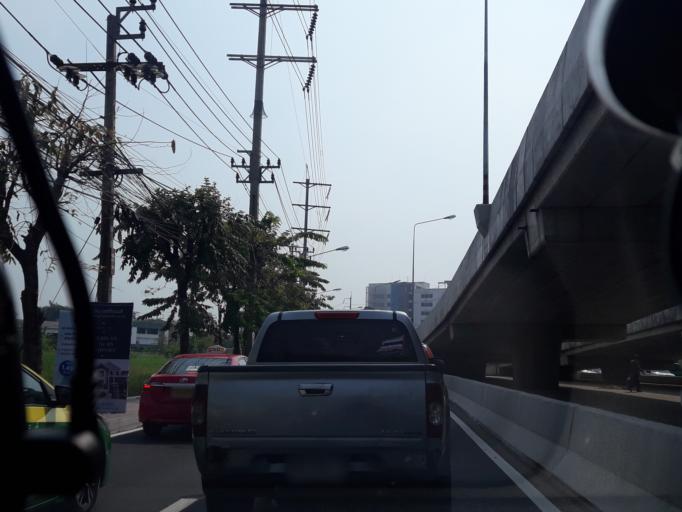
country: TH
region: Bangkok
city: Khan Na Yao
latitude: 13.8141
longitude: 100.6884
